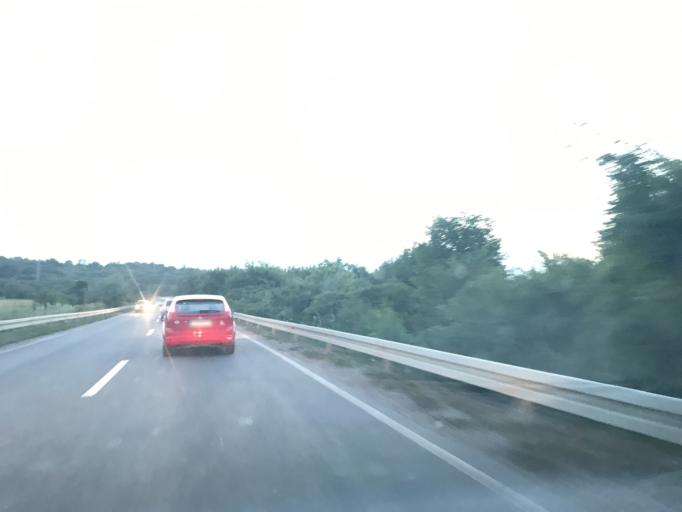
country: RS
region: Central Serbia
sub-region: Branicevski Okrug
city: Pozarevac
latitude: 44.6462
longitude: 21.2170
